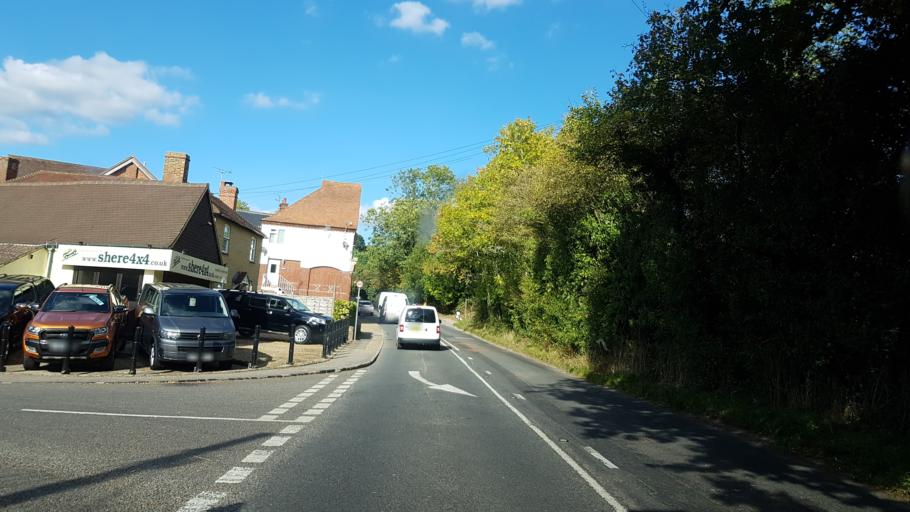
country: GB
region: England
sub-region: Surrey
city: Chiddingfold
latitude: 51.0531
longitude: -0.6438
